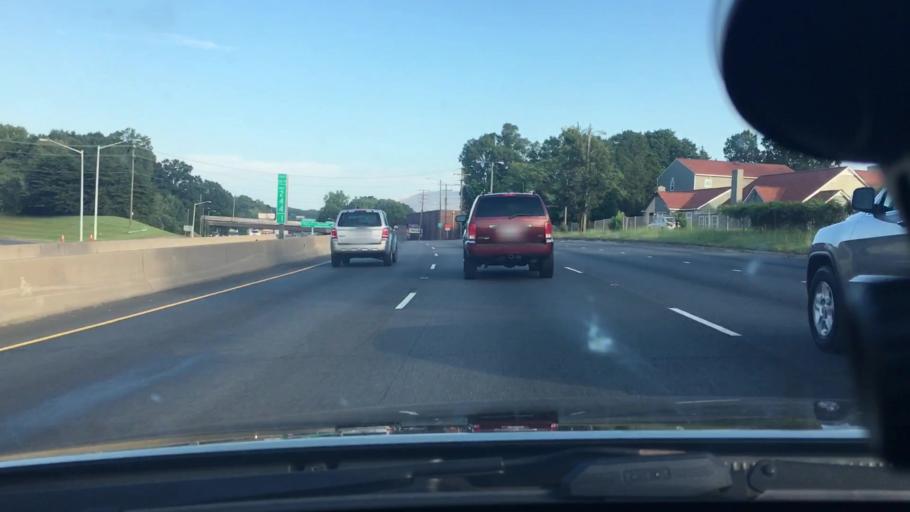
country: US
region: North Carolina
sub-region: Mecklenburg County
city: Charlotte
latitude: 35.2088
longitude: -80.7998
